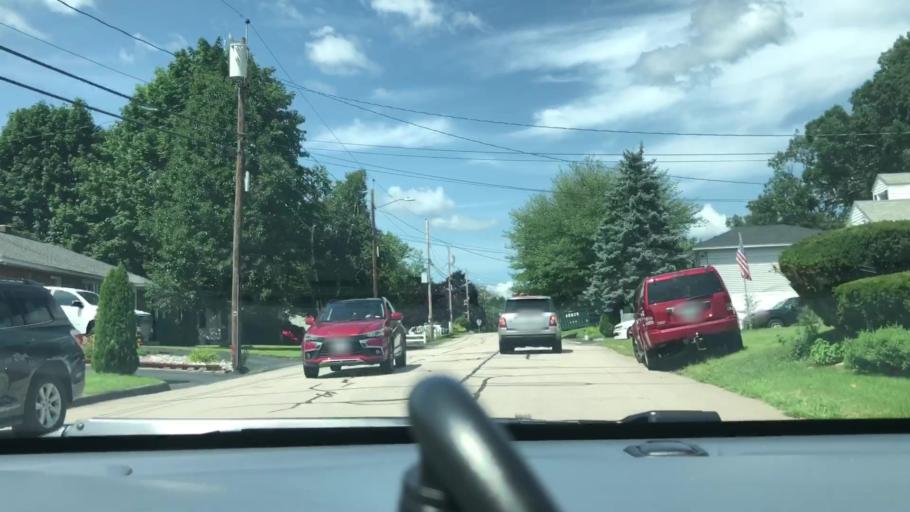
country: US
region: New Hampshire
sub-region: Hillsborough County
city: Pinardville
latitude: 42.9954
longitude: -71.4904
